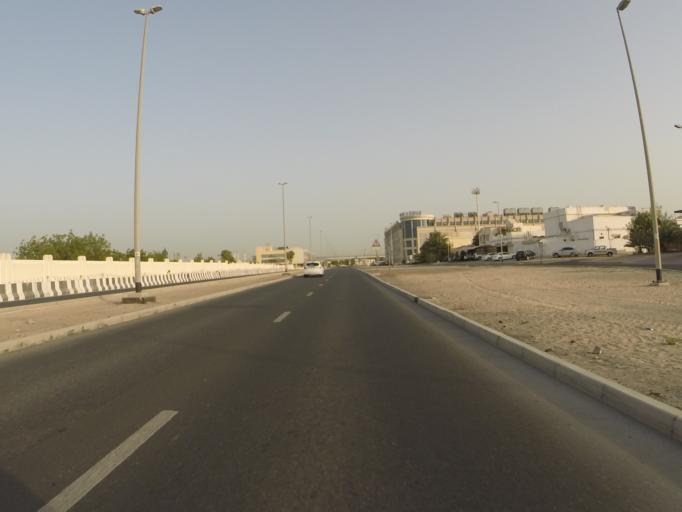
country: AE
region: Dubai
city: Dubai
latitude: 25.1667
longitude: 55.2436
